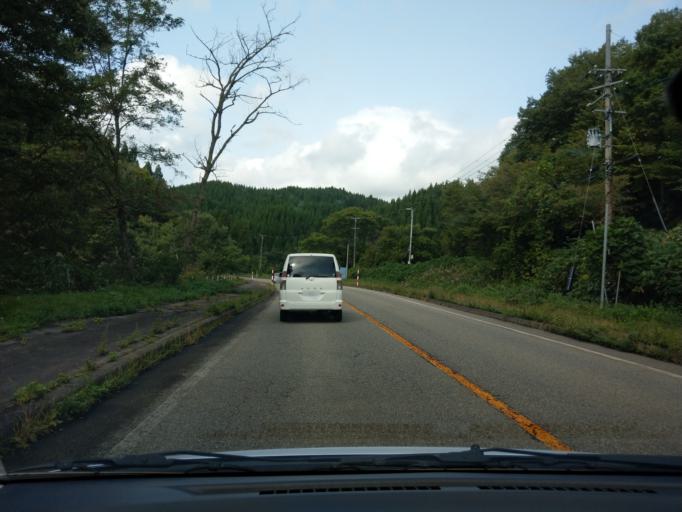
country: JP
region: Akita
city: Omagari
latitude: 39.4339
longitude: 140.3765
